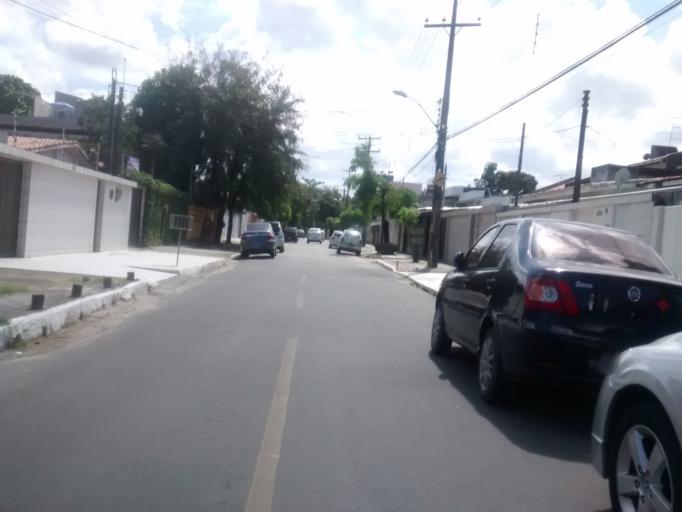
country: BR
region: Pernambuco
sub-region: Recife
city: Recife
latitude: -8.0960
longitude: -34.9121
